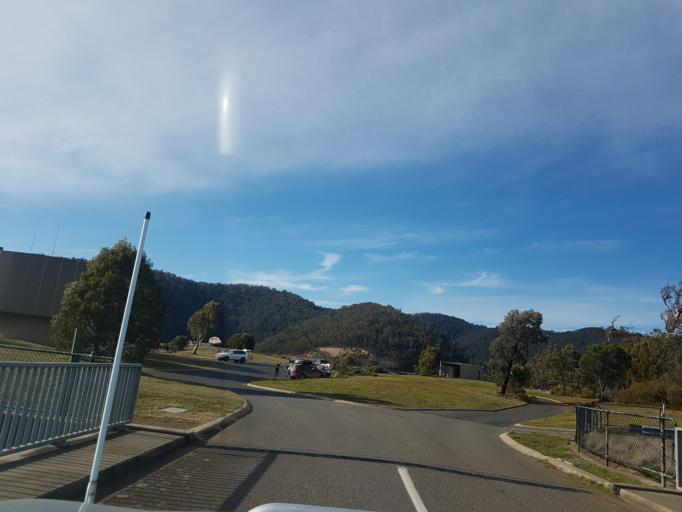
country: AU
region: Victoria
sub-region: Latrobe
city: Moe
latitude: -37.8441
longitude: 146.3983
